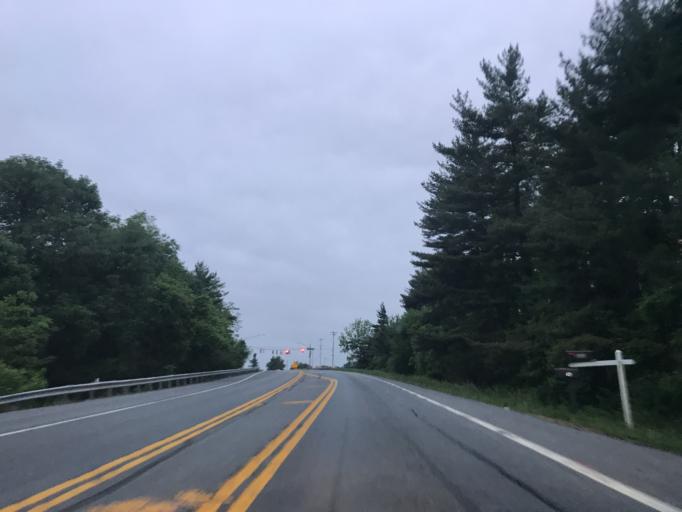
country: US
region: Maryland
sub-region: Frederick County
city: Linganore
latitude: 39.4379
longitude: -77.2530
